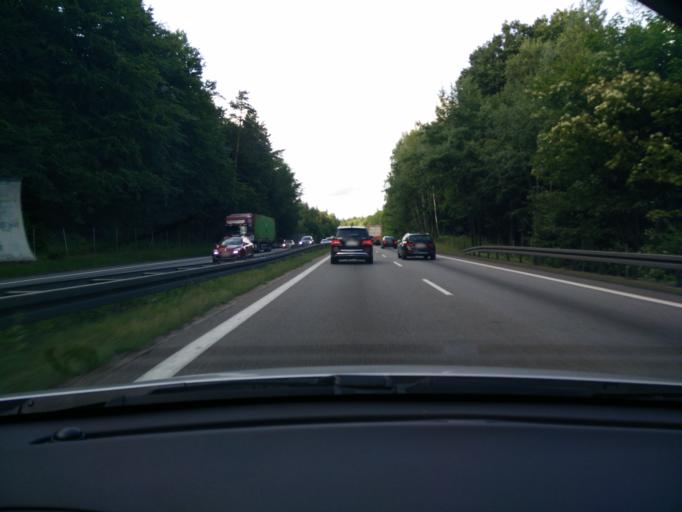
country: PL
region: Pomeranian Voivodeship
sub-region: Gdynia
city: Wielki Kack
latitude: 54.4416
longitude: 18.4898
